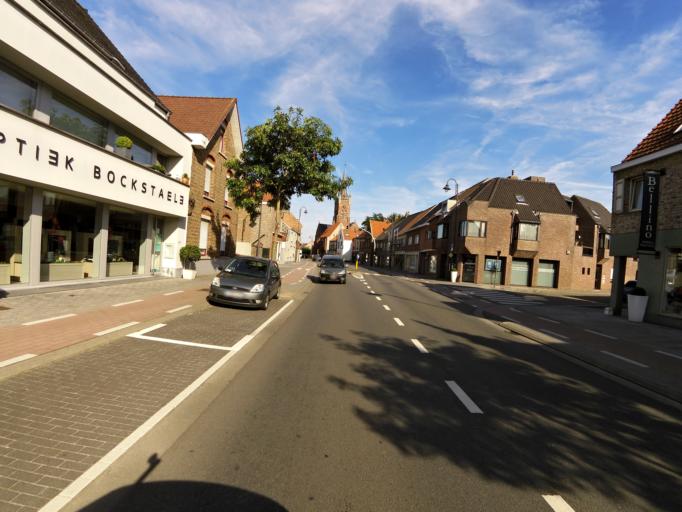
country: BE
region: Flanders
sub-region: Provincie West-Vlaanderen
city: Damme
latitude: 51.2017
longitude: 3.3202
